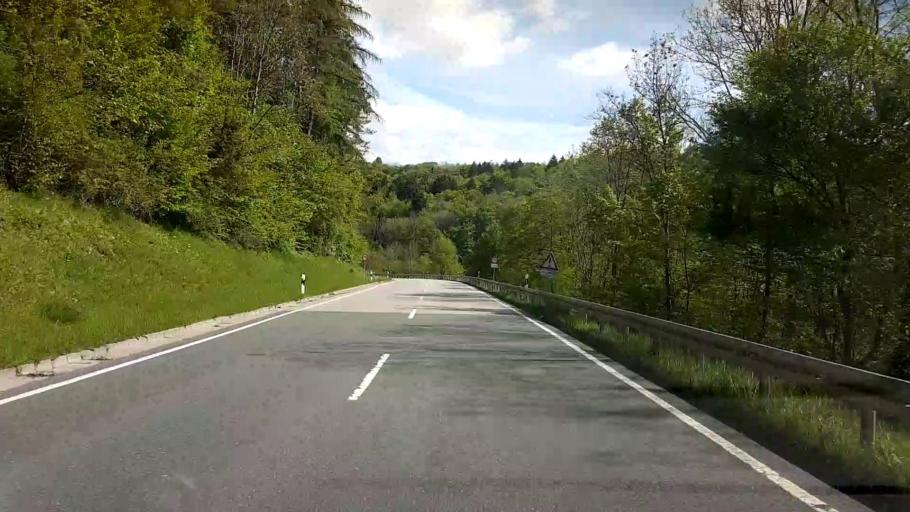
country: DE
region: Bavaria
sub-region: Upper Franconia
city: Ebermannstadt
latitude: 49.8068
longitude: 11.1471
